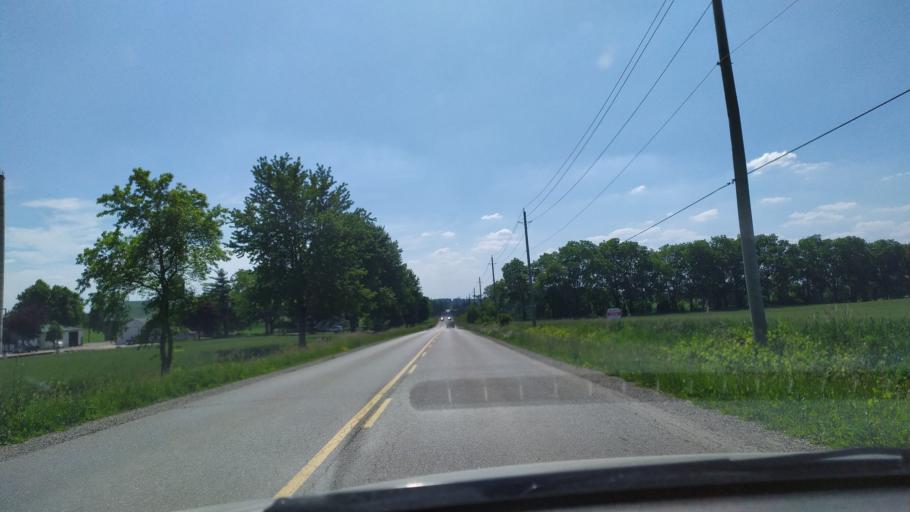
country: CA
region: Ontario
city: Kitchener
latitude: 43.3764
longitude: -80.5234
